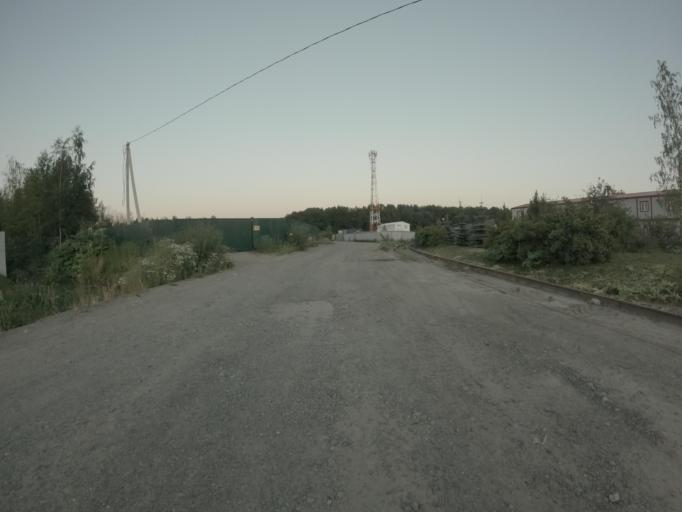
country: RU
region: Leningrad
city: Yanino Vtoroye
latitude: 59.9370
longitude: 30.5505
